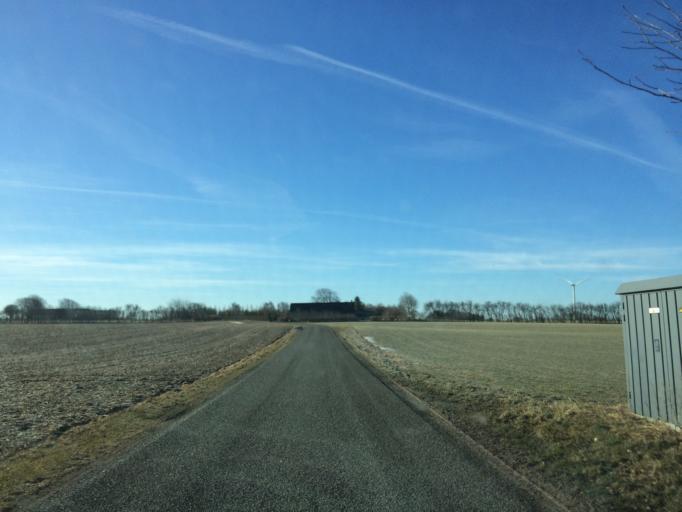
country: DK
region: North Denmark
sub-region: Mariagerfjord Kommune
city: Hobro
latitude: 56.6377
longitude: 9.6421
